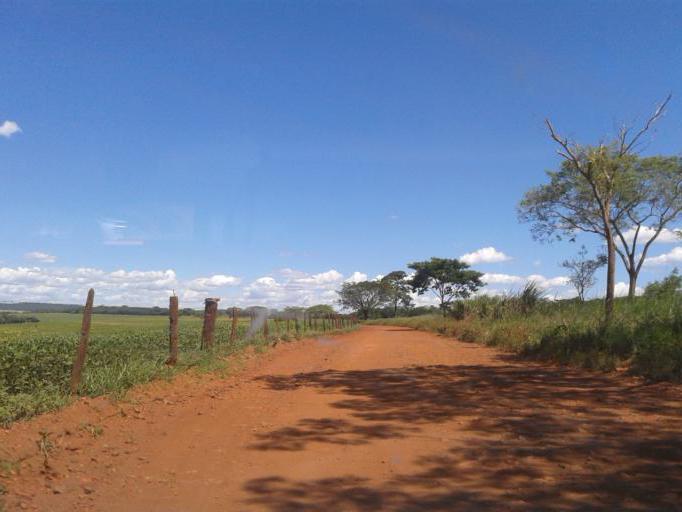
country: BR
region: Minas Gerais
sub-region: Capinopolis
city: Capinopolis
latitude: -18.5960
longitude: -49.6225
